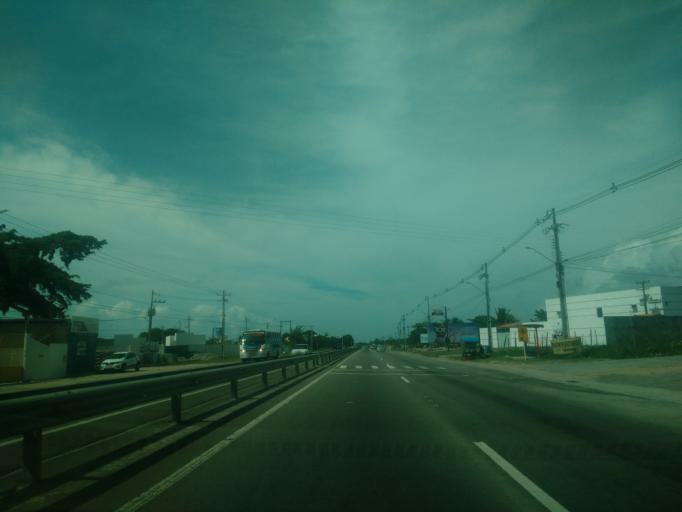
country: BR
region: Alagoas
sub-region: Marechal Deodoro
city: Marechal Deodoro
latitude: -9.7480
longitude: -35.8389
